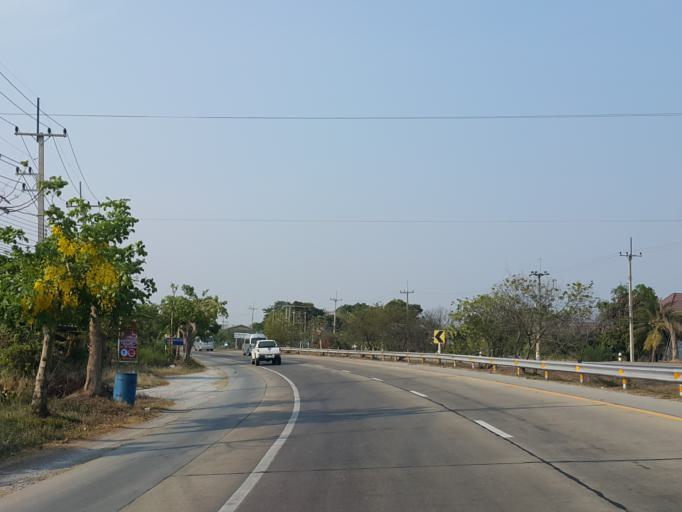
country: TH
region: Suphan Buri
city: Sam Chuk
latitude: 14.7938
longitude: 100.1063
